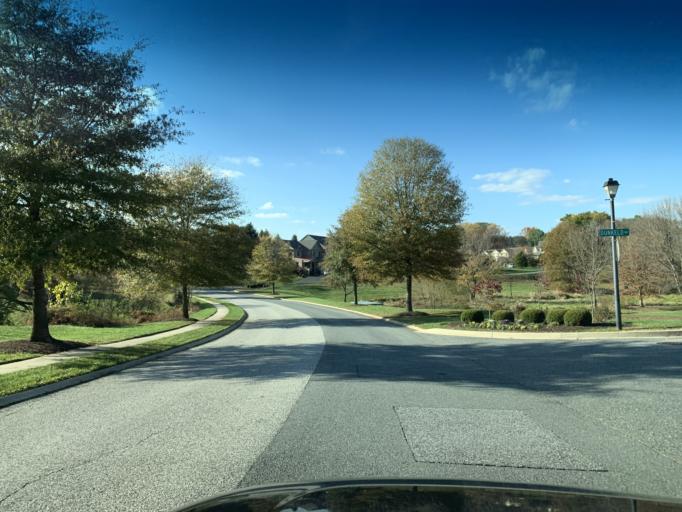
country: US
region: Maryland
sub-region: Harford County
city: Bel Air South
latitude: 39.5128
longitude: -76.2996
